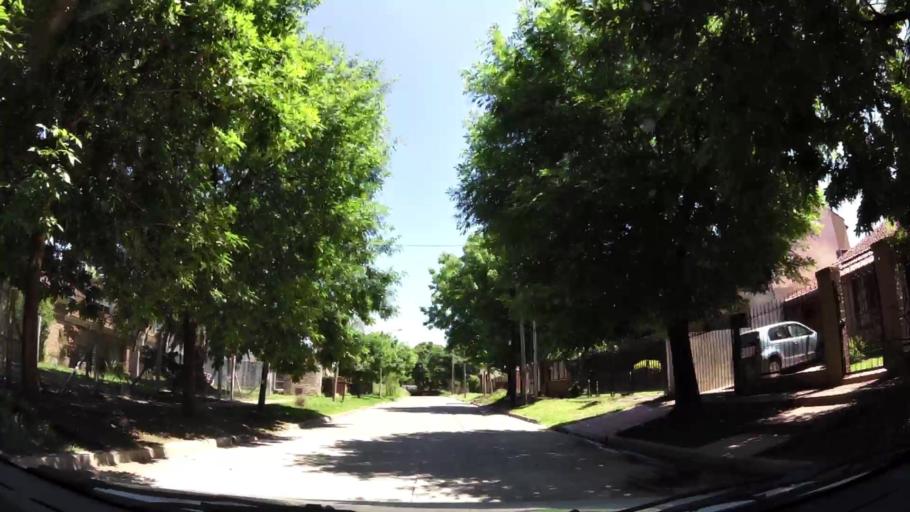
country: AR
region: Buenos Aires
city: Ituzaingo
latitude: -34.6612
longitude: -58.6855
